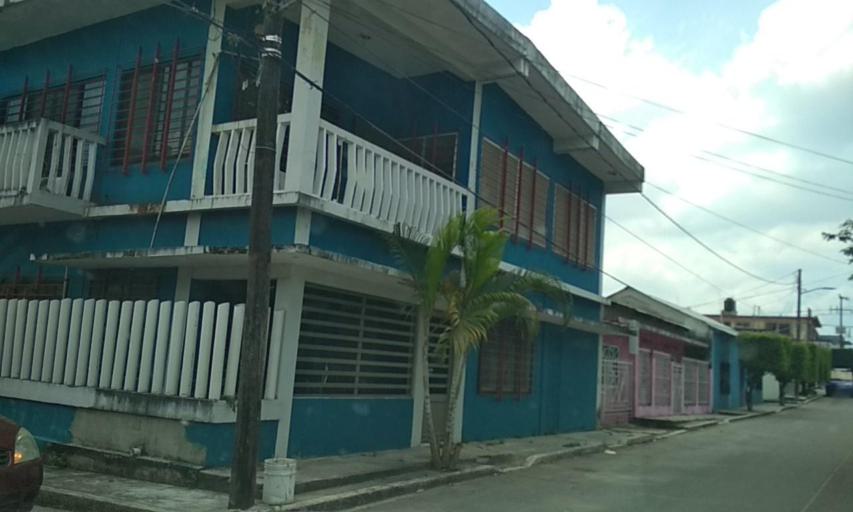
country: MX
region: Veracruz
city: Las Choapas
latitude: 17.9156
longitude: -94.0901
